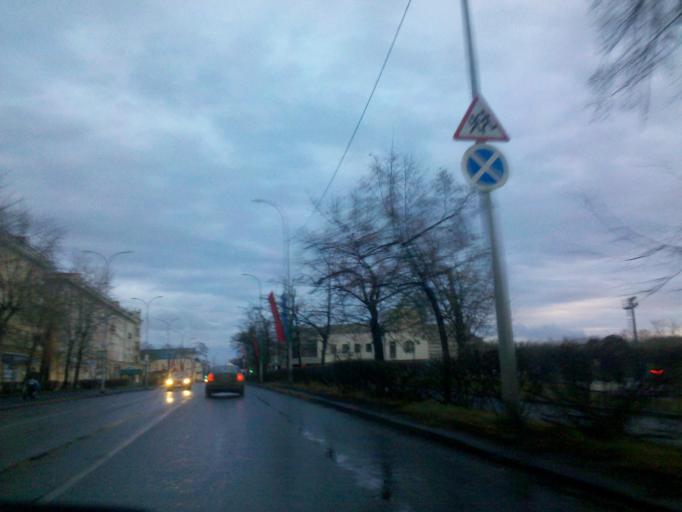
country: RU
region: Republic of Karelia
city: Petrozavodsk
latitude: 61.7879
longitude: 34.3757
